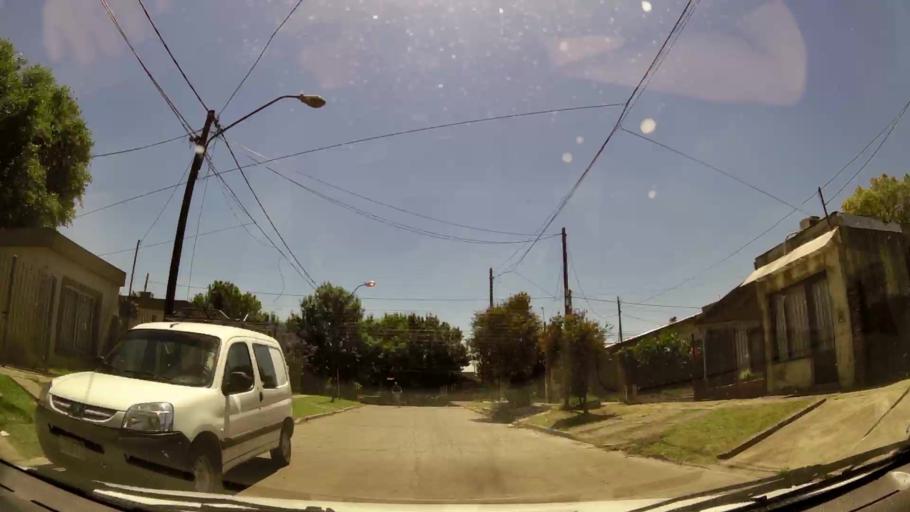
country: AR
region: Buenos Aires
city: Ituzaingo
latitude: -34.6604
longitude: -58.6858
